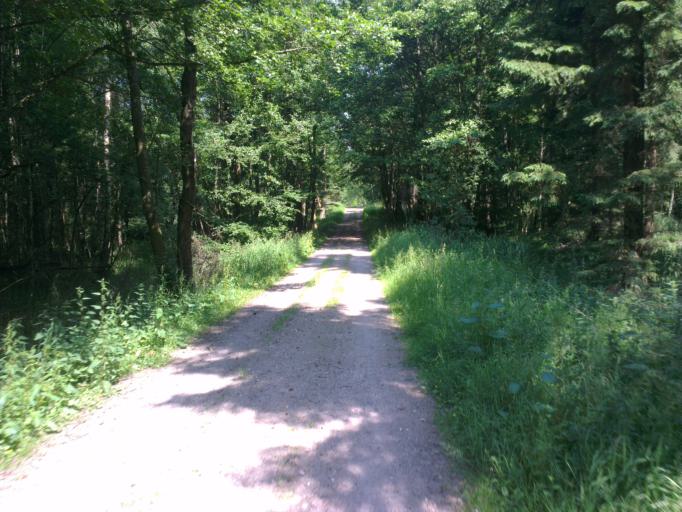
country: DK
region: Capital Region
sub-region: Allerod Kommune
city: Lillerod
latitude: 55.9242
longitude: 12.3616
